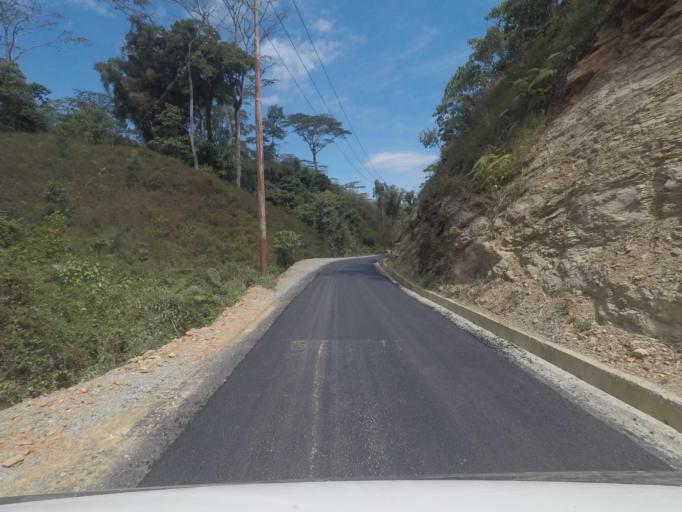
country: TL
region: Ermera
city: Gleno
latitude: -8.7527
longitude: 125.3383
